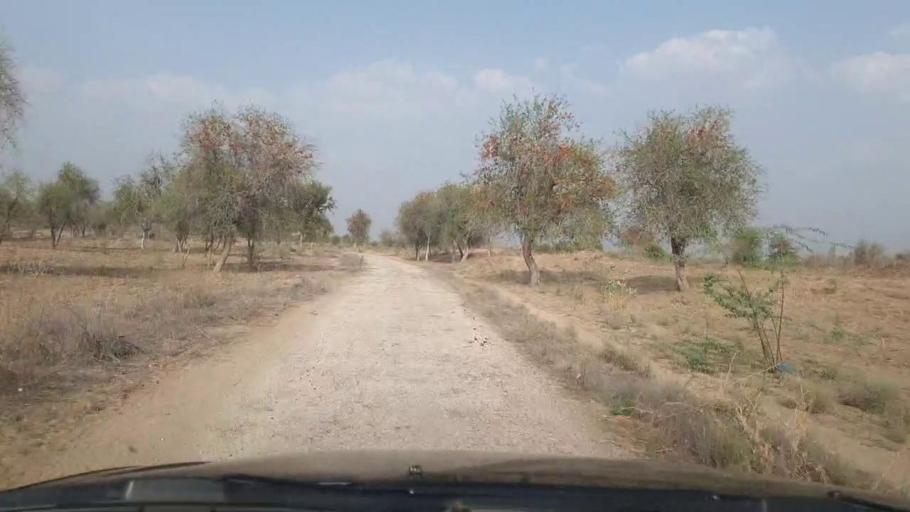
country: PK
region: Sindh
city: Islamkot
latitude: 25.0331
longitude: 70.5600
